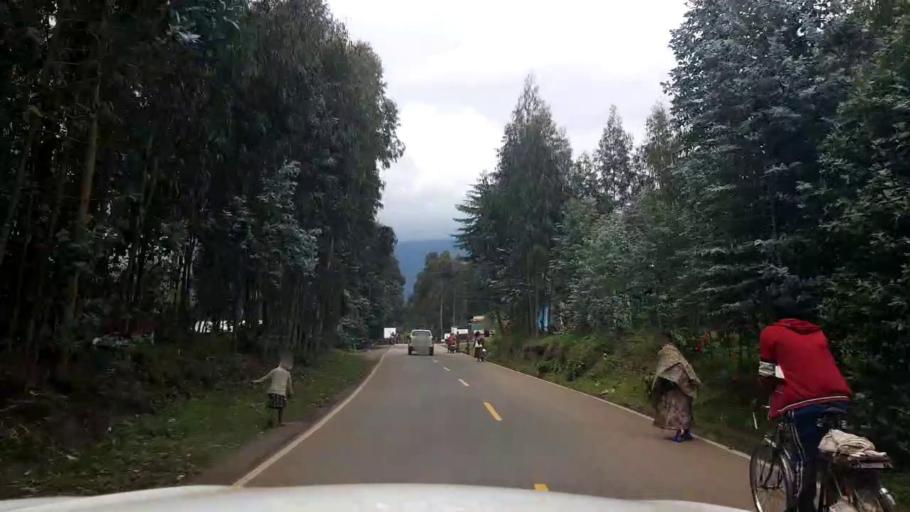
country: RW
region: Northern Province
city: Musanze
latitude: -1.4404
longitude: 29.5423
